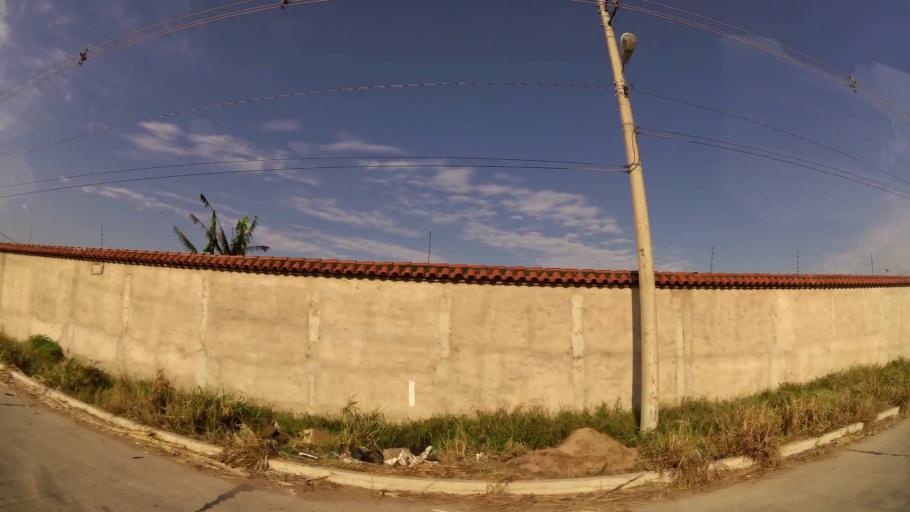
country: BO
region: Santa Cruz
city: Santa Cruz de la Sierra
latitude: -17.6801
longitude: -63.1533
